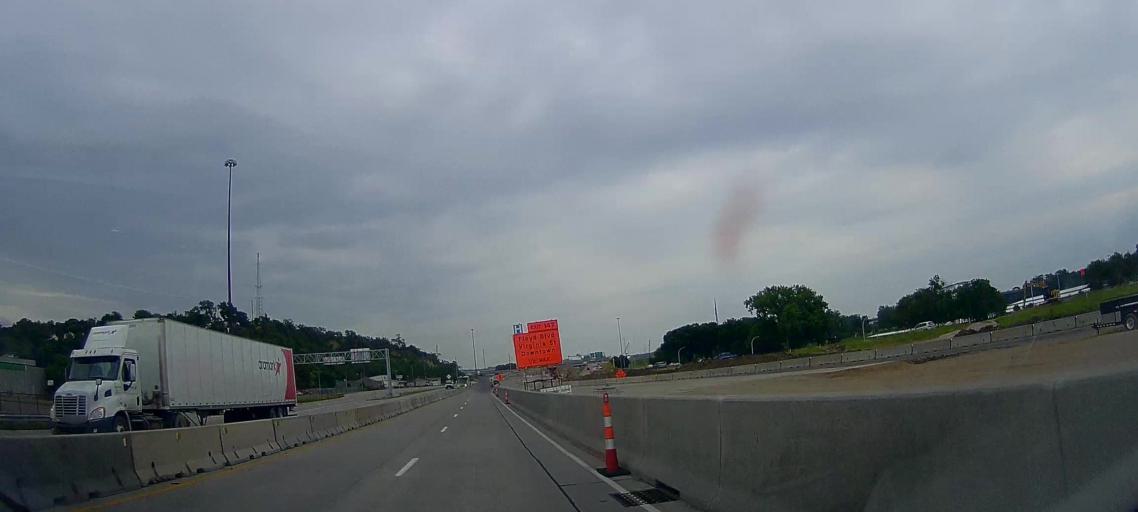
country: US
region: Nebraska
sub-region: Dakota County
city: South Sioux City
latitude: 42.4921
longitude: -96.4216
